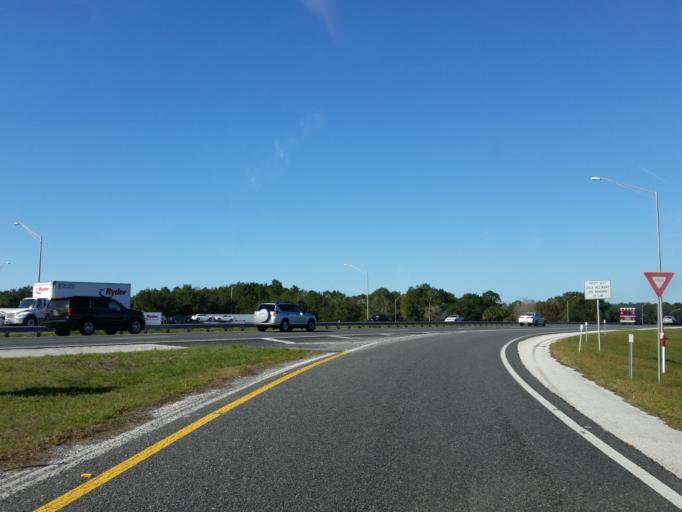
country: US
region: Florida
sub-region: Marion County
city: Ocala
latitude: 29.0953
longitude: -82.1846
